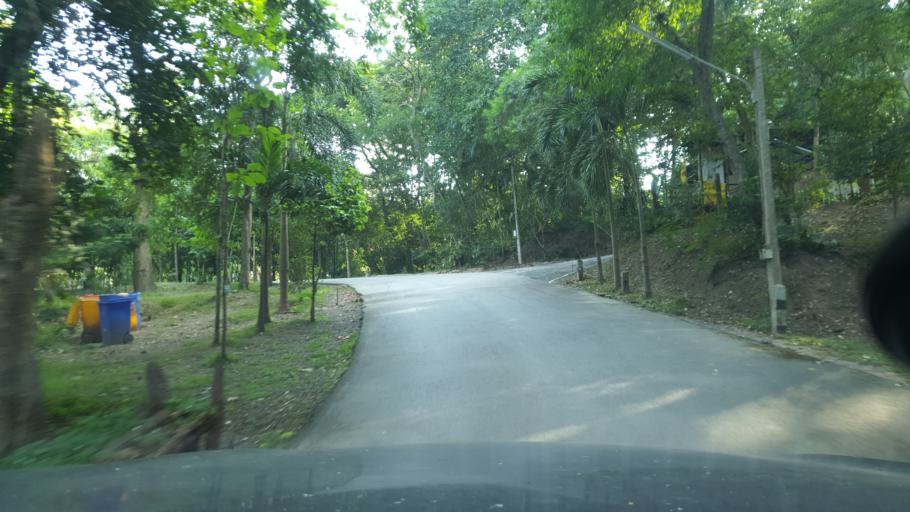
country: TH
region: Chiang Mai
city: Chiang Mai
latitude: 18.8281
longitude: 98.9525
